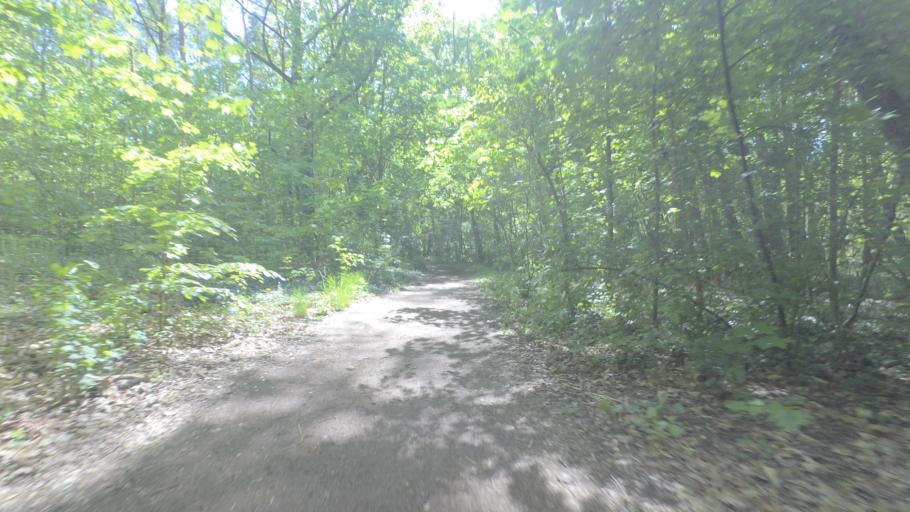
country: DE
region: Brandenburg
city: Erkner
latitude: 52.4299
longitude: 13.7666
